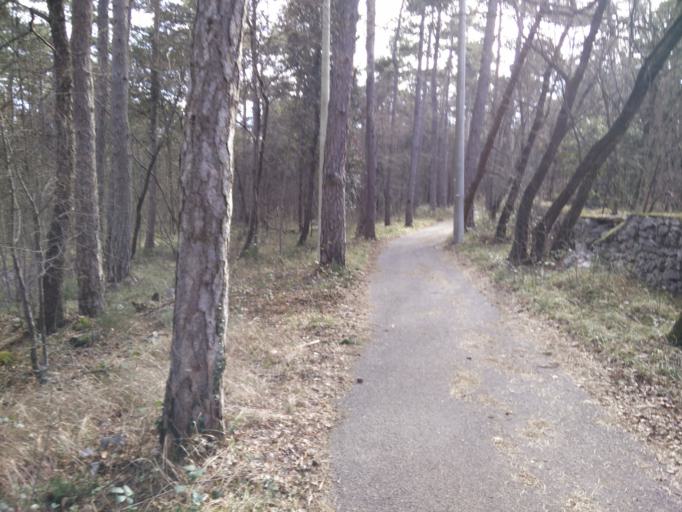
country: IT
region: Friuli Venezia Giulia
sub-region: Provincia di Trieste
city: Santa Croce
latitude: 45.7283
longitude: 13.6987
